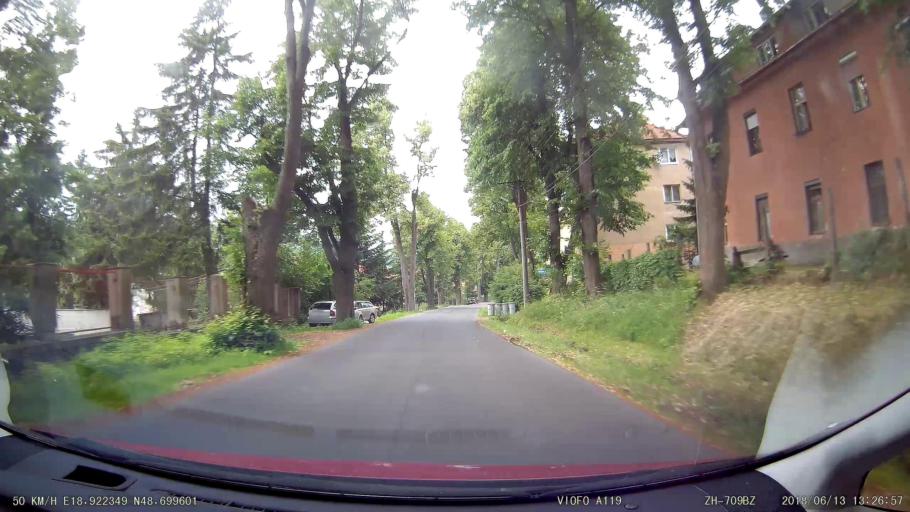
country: SK
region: Banskobystricky
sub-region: Okres Ziar nad Hronom
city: Kremnica
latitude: 48.6997
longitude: 18.9223
